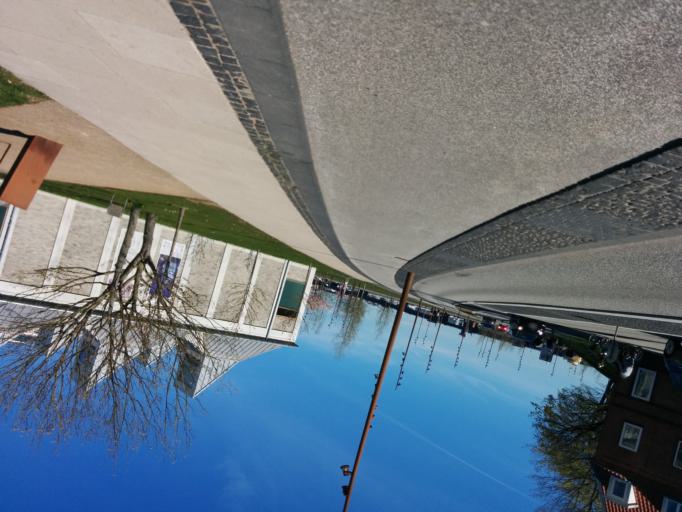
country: DK
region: North Denmark
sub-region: Alborg Kommune
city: Aalborg
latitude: 57.0489
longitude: 9.9261
